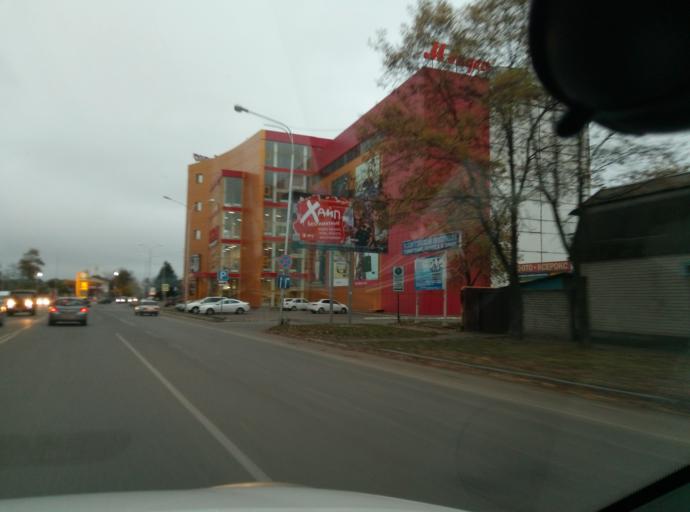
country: RU
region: Stavropol'skiy
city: Yessentuki
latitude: 44.0389
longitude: 42.8685
